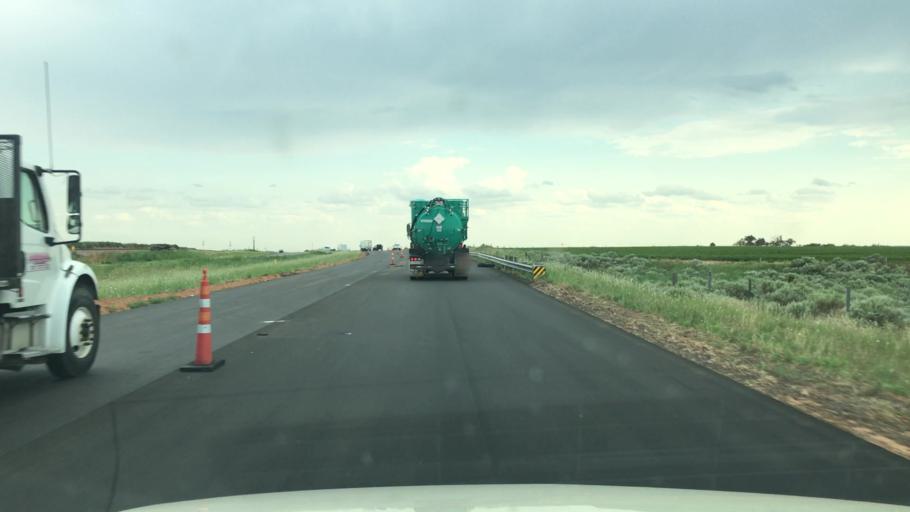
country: US
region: Texas
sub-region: Hall County
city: Memphis
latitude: 34.6336
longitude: -100.4766
